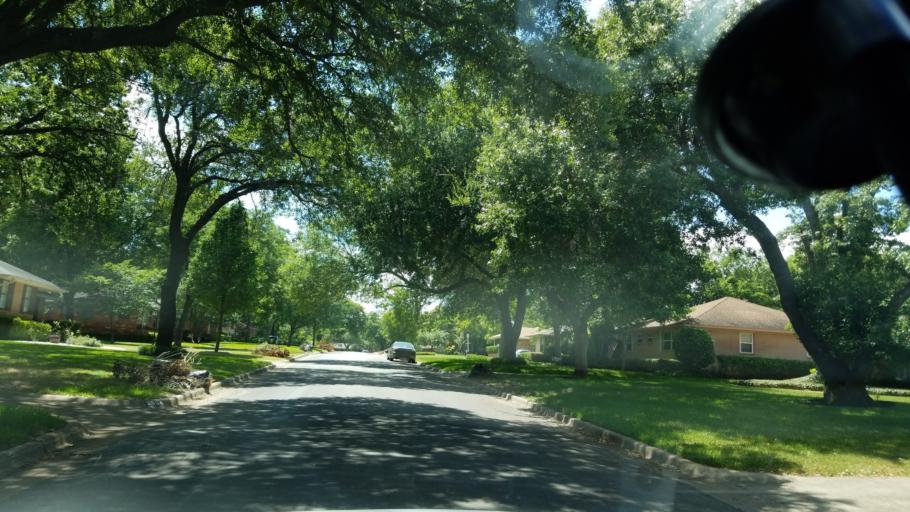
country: US
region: Texas
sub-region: Dallas County
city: Cockrell Hill
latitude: 32.7021
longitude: -96.8658
